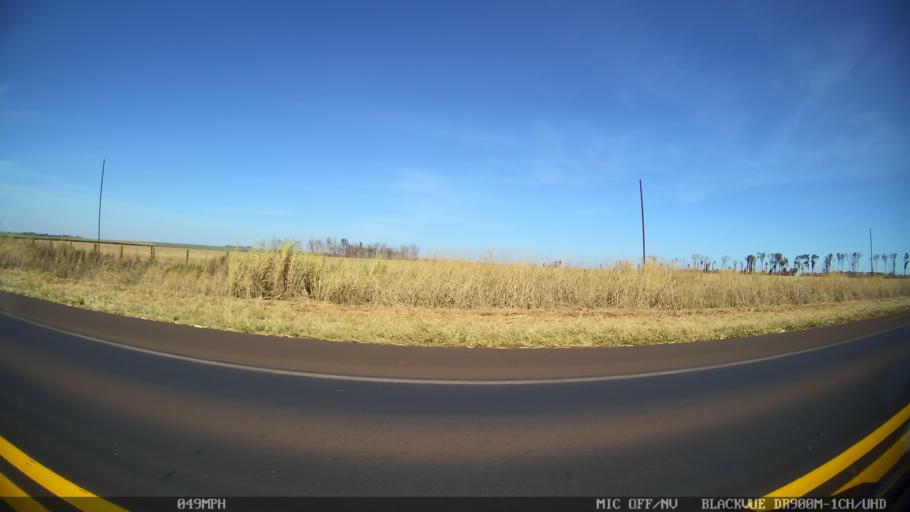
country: BR
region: Sao Paulo
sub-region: Barretos
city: Barretos
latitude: -20.4858
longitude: -48.5132
